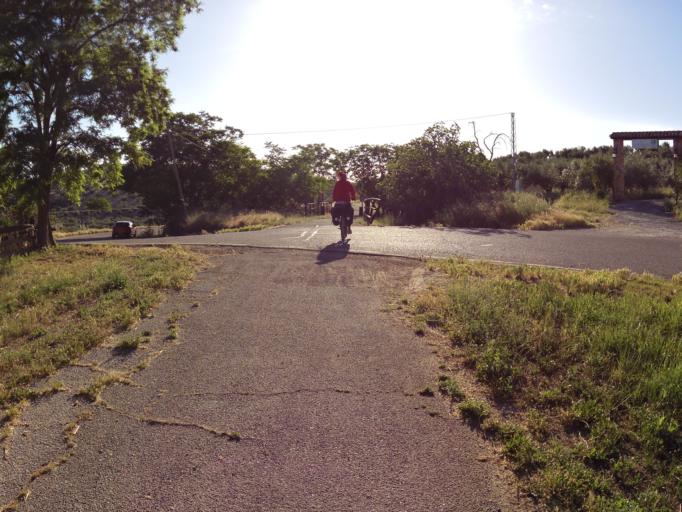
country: ES
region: Andalusia
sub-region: Province of Cordoba
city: Luque
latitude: 37.5733
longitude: -4.2689
